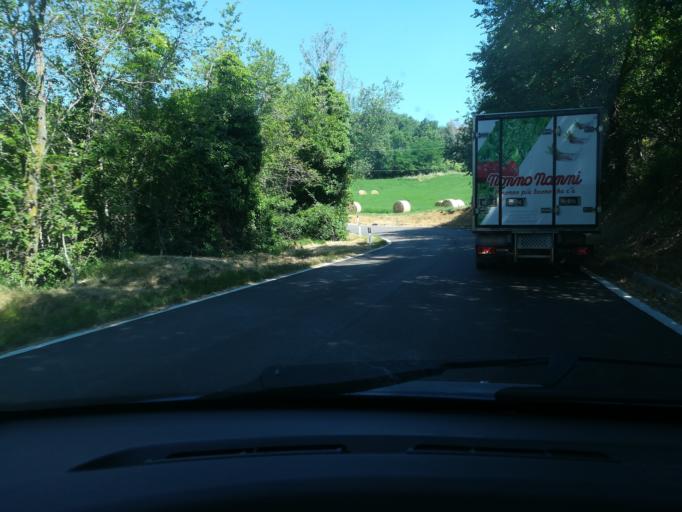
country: IT
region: The Marches
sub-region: Provincia di Macerata
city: San Ginesio
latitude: 43.1107
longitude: 13.3496
